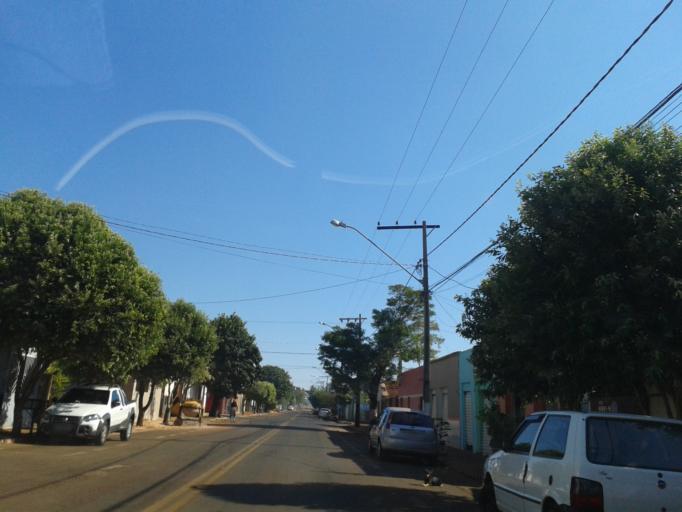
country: BR
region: Minas Gerais
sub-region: Capinopolis
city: Capinopolis
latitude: -18.5139
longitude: -49.5021
